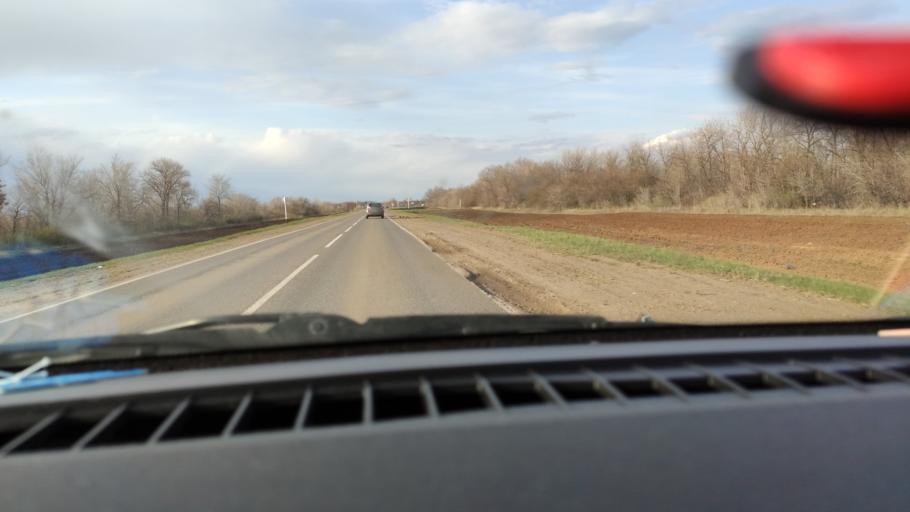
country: RU
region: Saratov
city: Privolzhskiy
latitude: 51.3434
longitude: 46.0420
